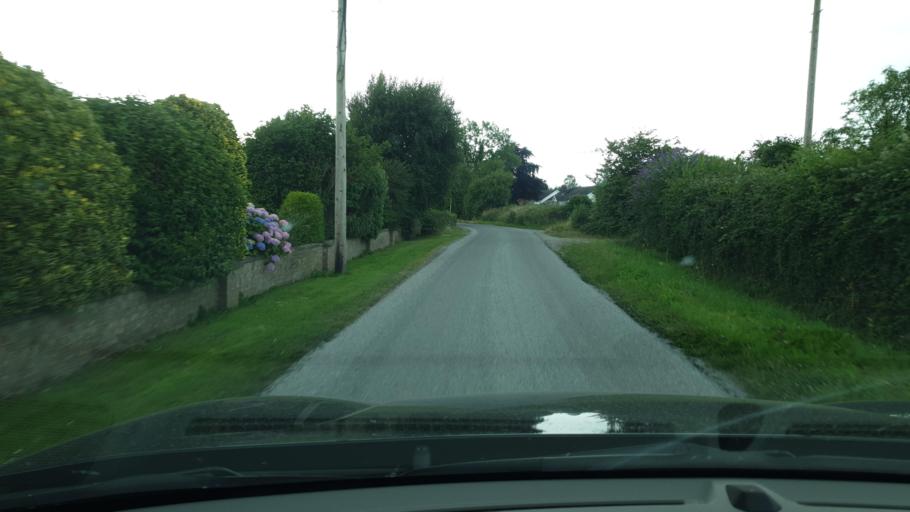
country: IE
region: Leinster
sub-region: An Mhi
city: Ratoath
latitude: 53.4932
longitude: -6.5016
